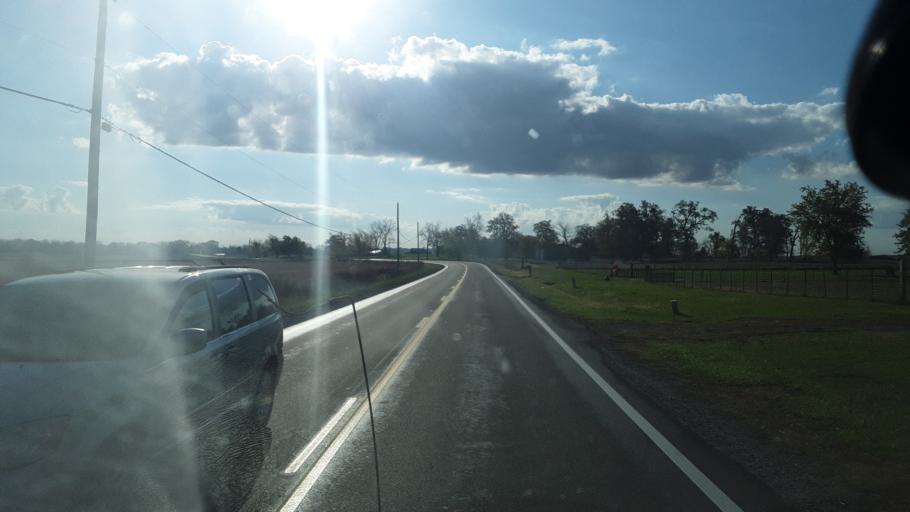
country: US
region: Ohio
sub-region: Fayette County
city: Jeffersonville
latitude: 39.5901
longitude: -83.5076
